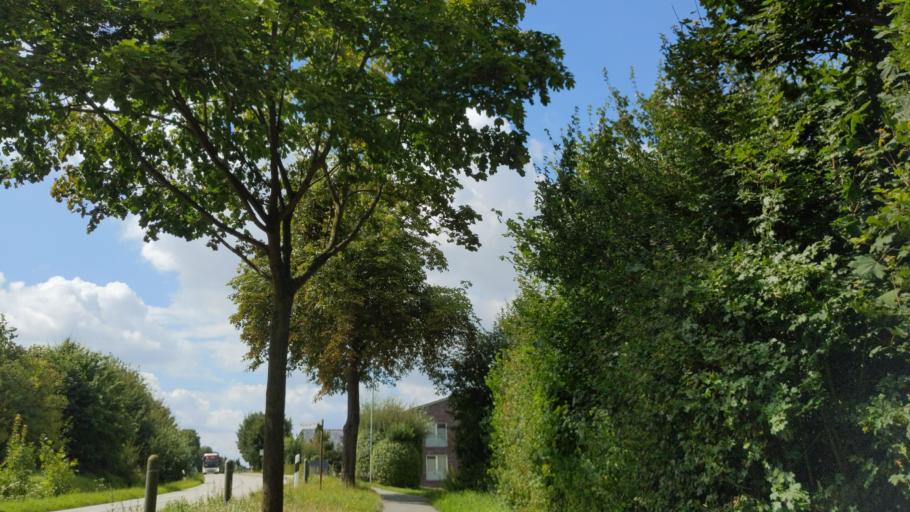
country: DE
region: Schleswig-Holstein
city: Hamberge
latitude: 53.8399
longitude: 10.5895
